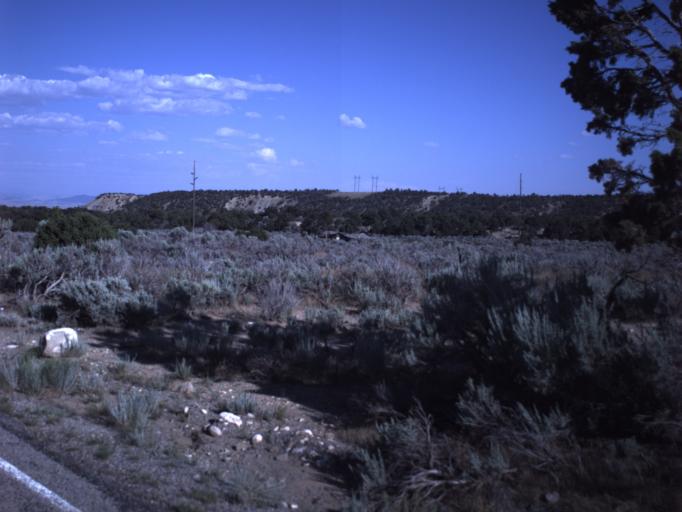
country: US
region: Utah
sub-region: Emery County
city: Huntington
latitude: 39.4842
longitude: -110.9941
